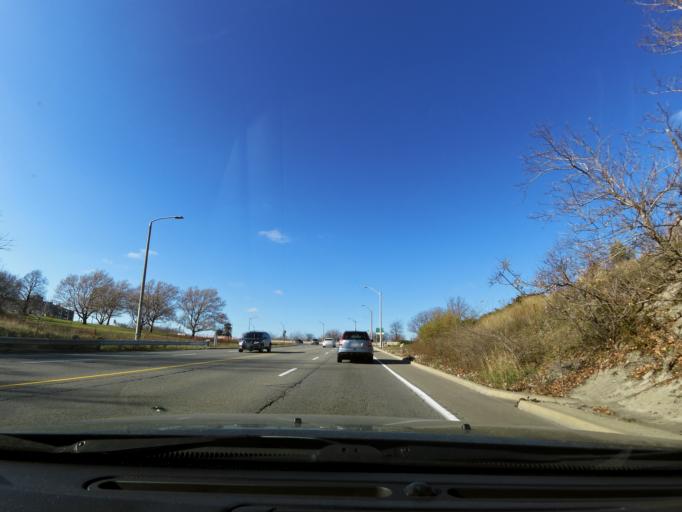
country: CA
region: Ontario
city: Hamilton
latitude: 43.2440
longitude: -79.8619
